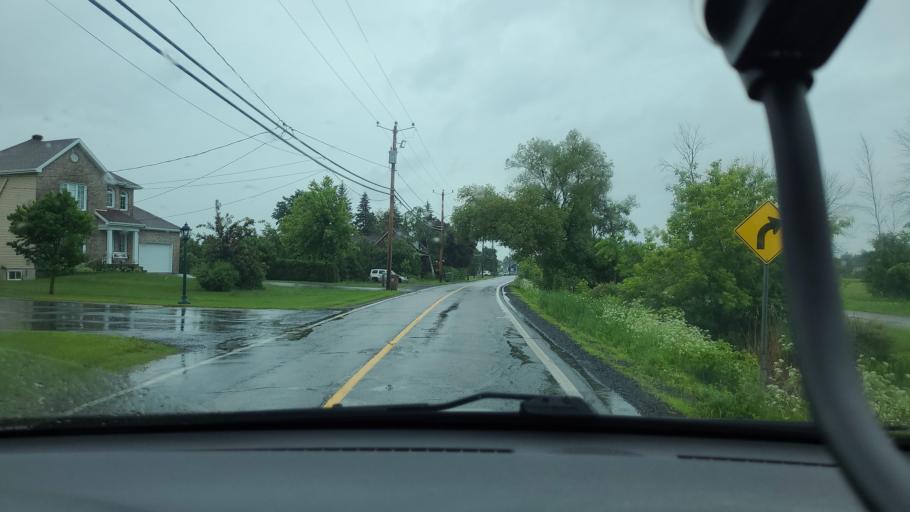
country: CA
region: Quebec
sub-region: Monteregie
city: Saint-Basile-le-Grand
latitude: 45.5348
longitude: -73.2789
